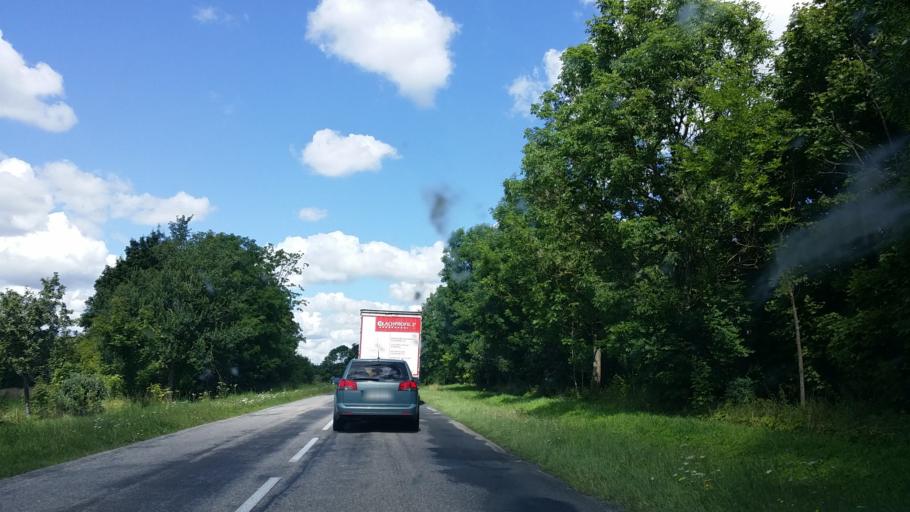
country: PL
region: West Pomeranian Voivodeship
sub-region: Powiat swidwinski
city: Swidwin
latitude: 53.8342
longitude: 15.7471
